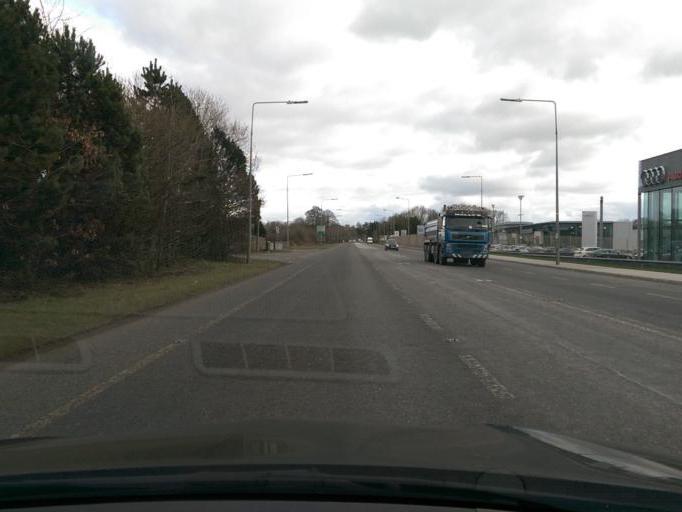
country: IE
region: Leinster
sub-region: An Iarmhi
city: Athlone
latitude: 53.4055
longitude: -7.8853
